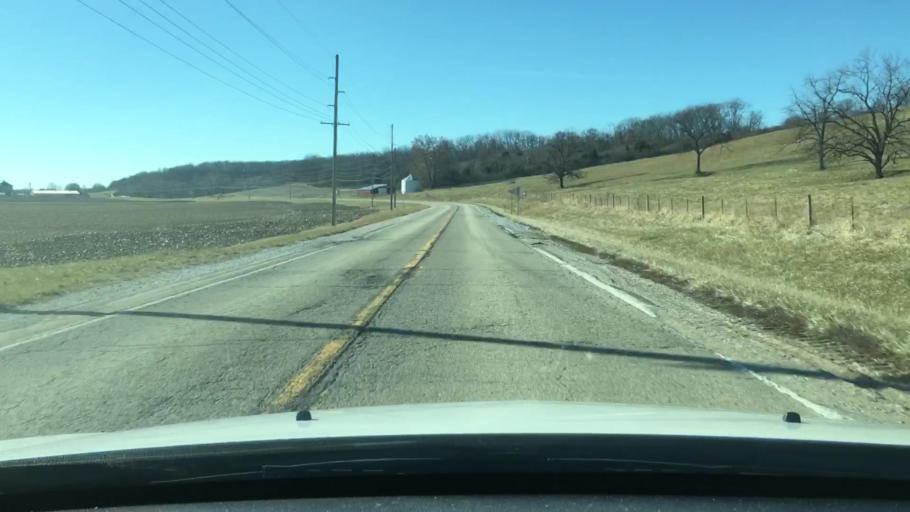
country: US
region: Illinois
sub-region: Fulton County
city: Astoria
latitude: 40.1747
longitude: -90.2839
